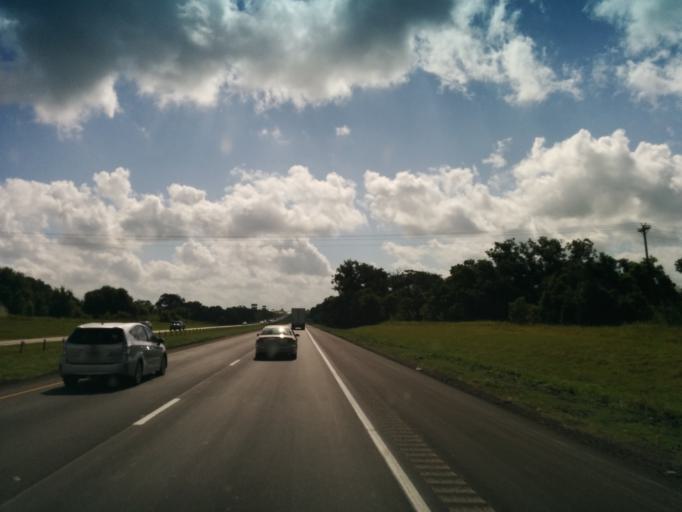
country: US
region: Texas
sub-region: Colorado County
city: Weimar
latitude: 29.6899
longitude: -96.8000
